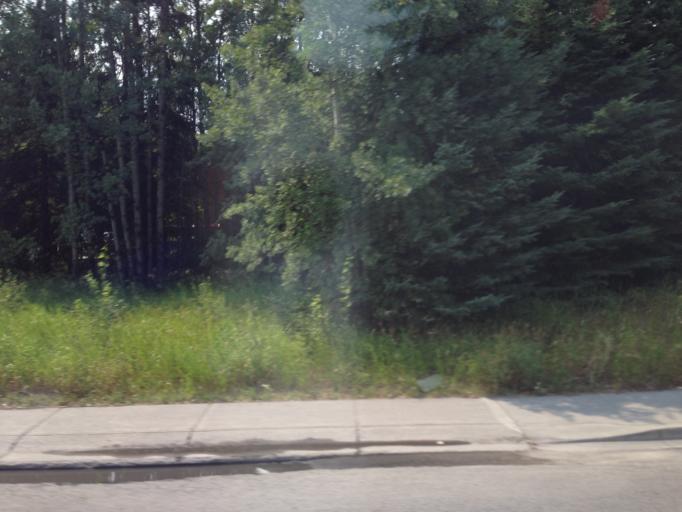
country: CA
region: Alberta
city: Canmore
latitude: 51.0961
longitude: -115.3591
